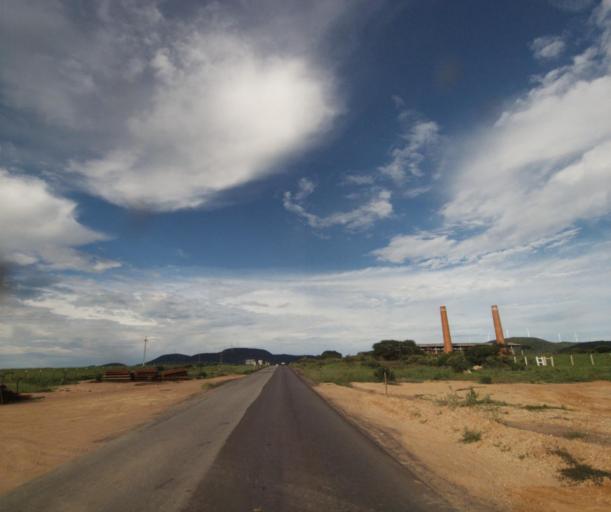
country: BR
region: Bahia
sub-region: Guanambi
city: Guanambi
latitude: -14.1834
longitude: -42.7368
